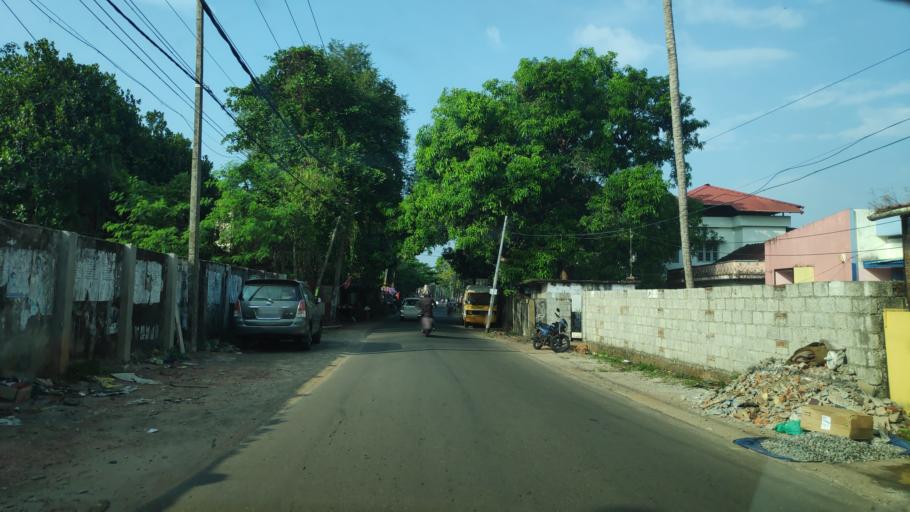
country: IN
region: Kerala
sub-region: Alappuzha
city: Alleppey
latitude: 9.4875
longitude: 76.3336
